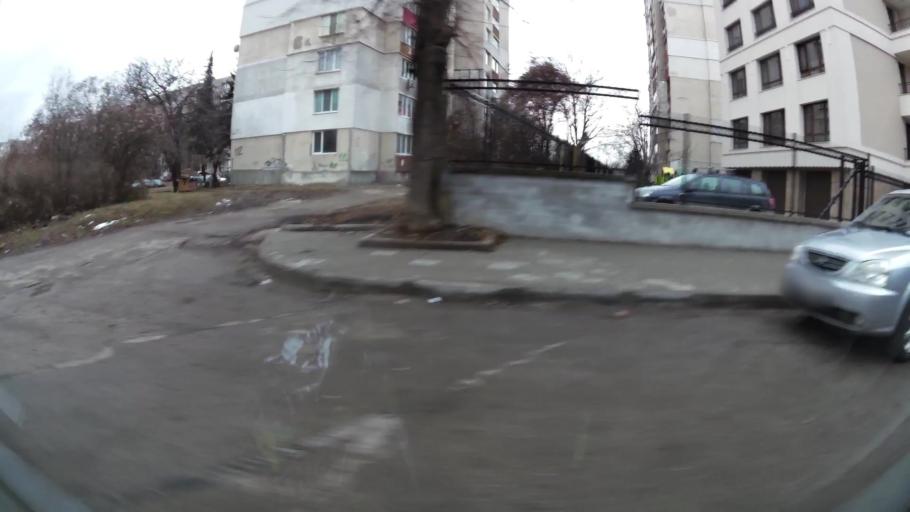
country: BG
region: Sofia-Capital
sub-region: Stolichna Obshtina
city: Sofia
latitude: 42.7256
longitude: 23.2936
